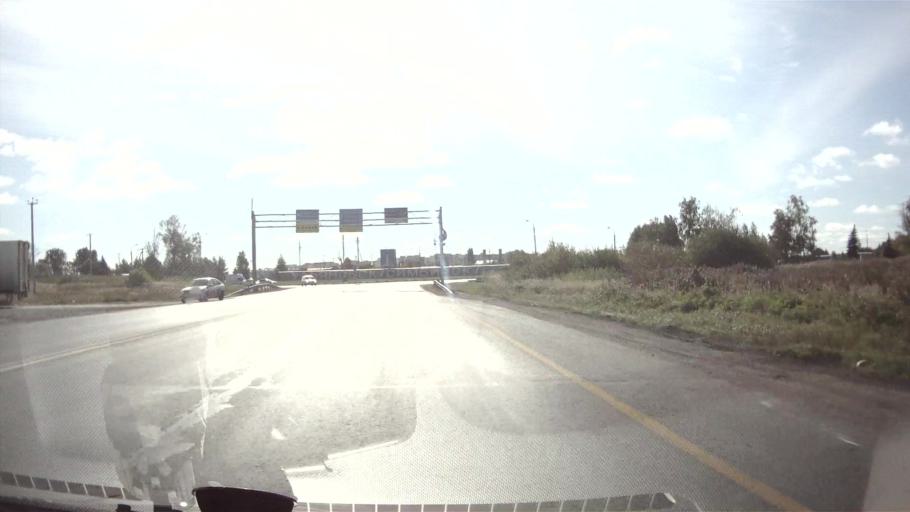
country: RU
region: Ulyanovsk
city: Isheyevka
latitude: 54.2925
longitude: 48.2529
